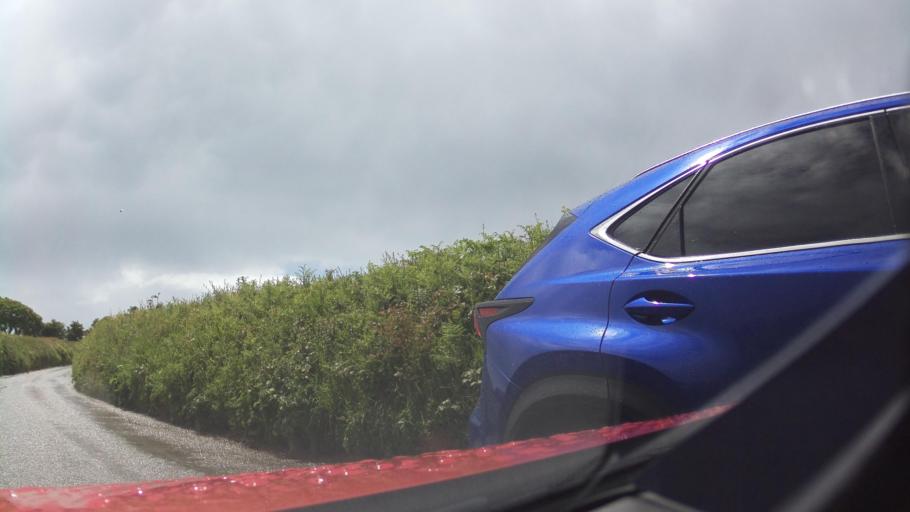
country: GB
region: England
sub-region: Devon
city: Dartmouth
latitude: 50.3524
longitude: -3.5379
